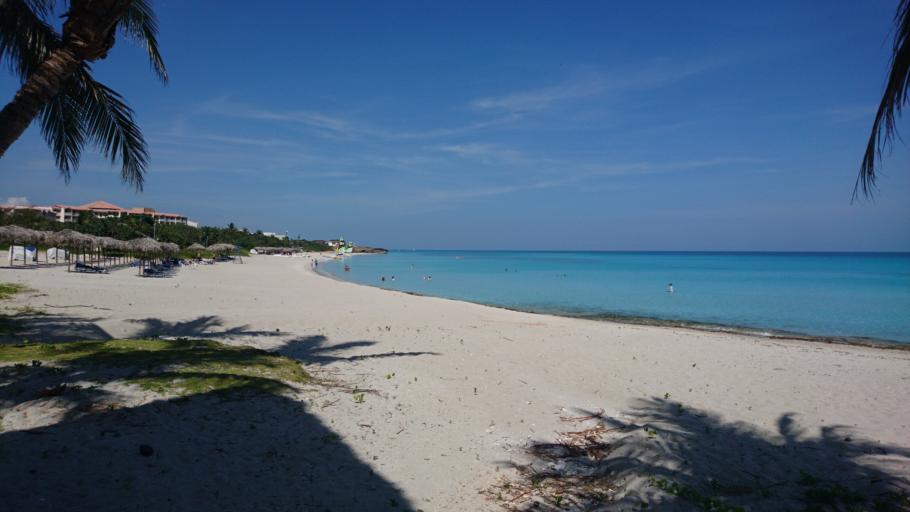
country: CU
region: Matanzas
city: Varadero
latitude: 23.1840
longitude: -81.1910
